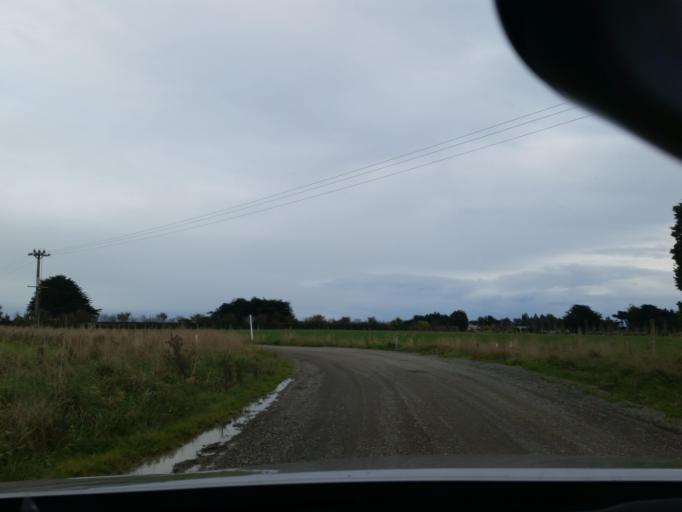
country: NZ
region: Southland
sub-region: Invercargill City
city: Invercargill
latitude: -46.2987
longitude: 168.3038
